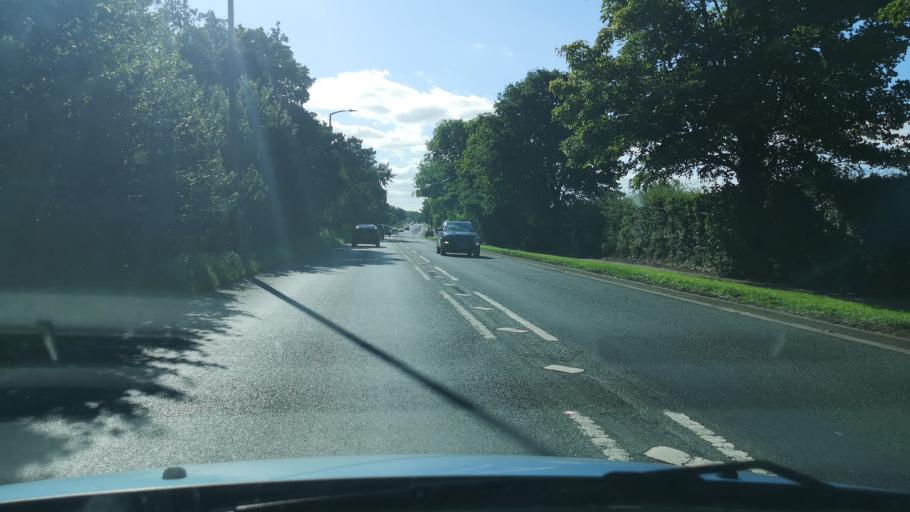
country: GB
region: England
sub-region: Doncaster
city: Armthorpe
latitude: 53.5582
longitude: -1.0422
